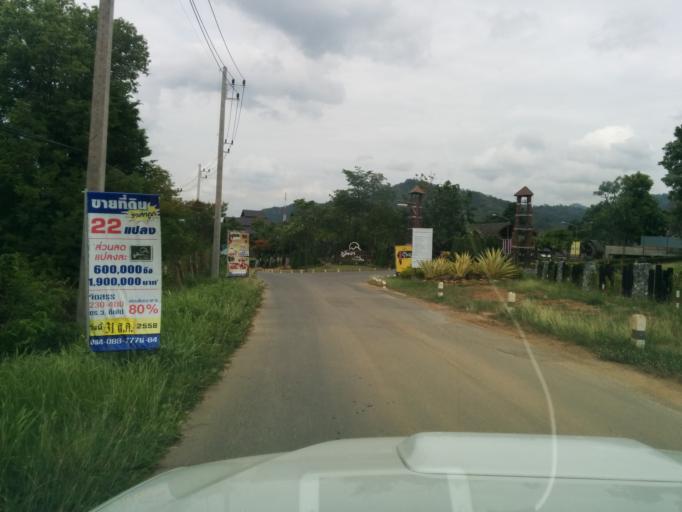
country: TH
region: Sara Buri
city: Muak Lek
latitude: 14.5604
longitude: 101.2539
